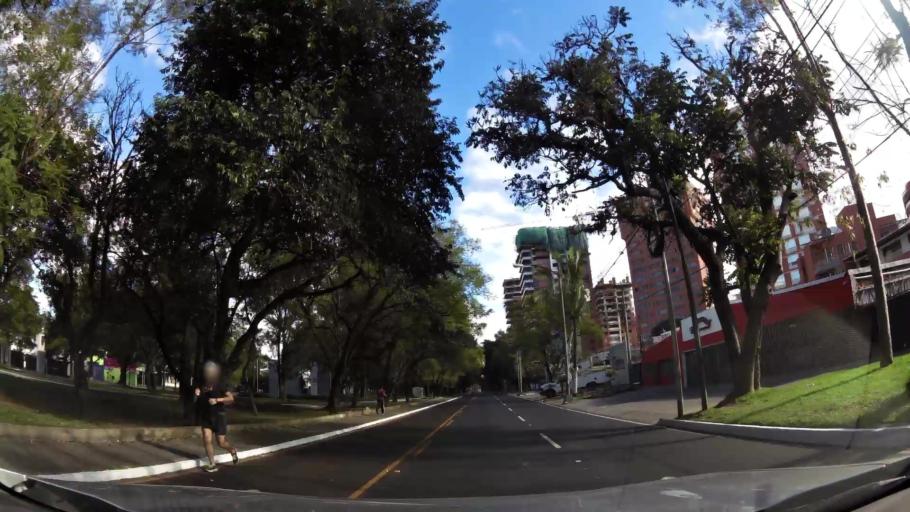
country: GT
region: Guatemala
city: Santa Catarina Pinula
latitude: 14.5749
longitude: -90.5239
